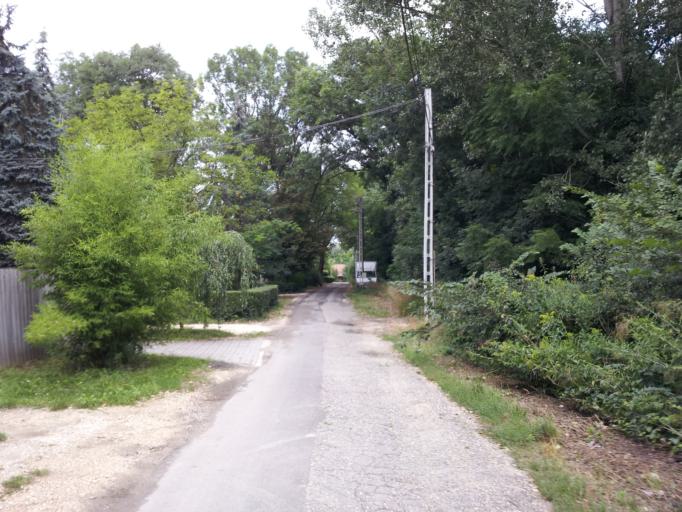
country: HU
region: Pest
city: Szigetujfalu
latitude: 47.2191
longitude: 18.9693
